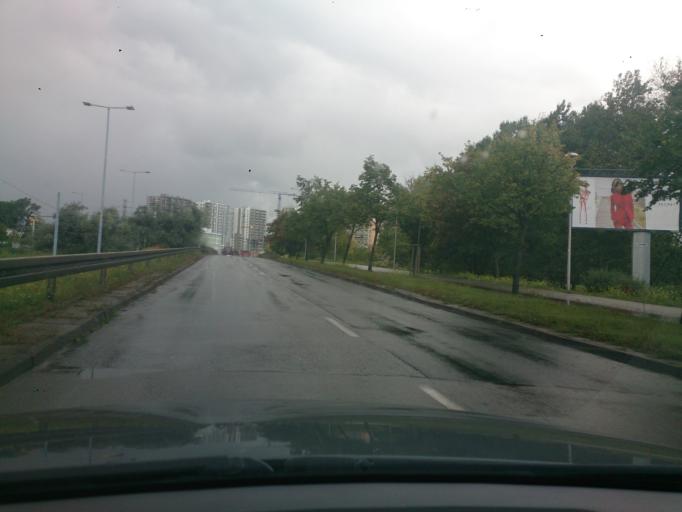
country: PL
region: Pomeranian Voivodeship
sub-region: Sopot
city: Sopot
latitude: 54.3975
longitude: 18.5969
